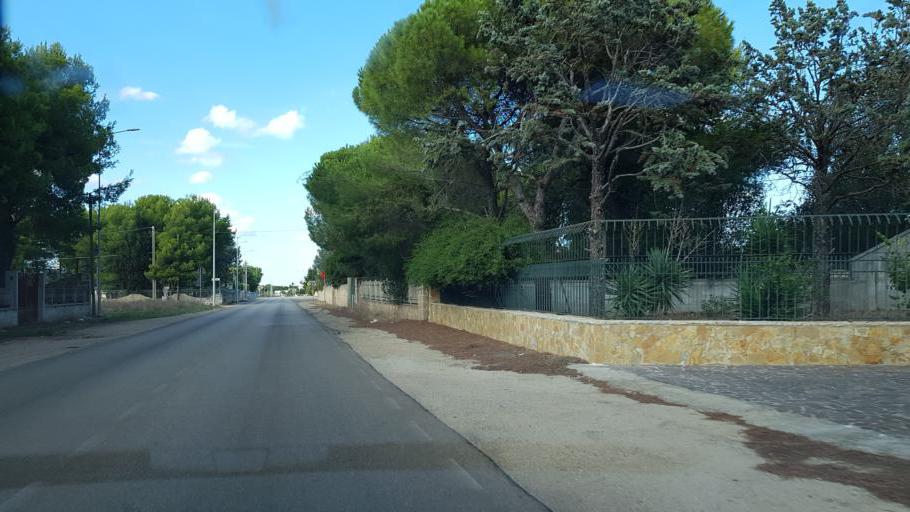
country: IT
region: Apulia
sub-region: Provincia di Lecce
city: Nardo
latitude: 40.1435
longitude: 18.0187
